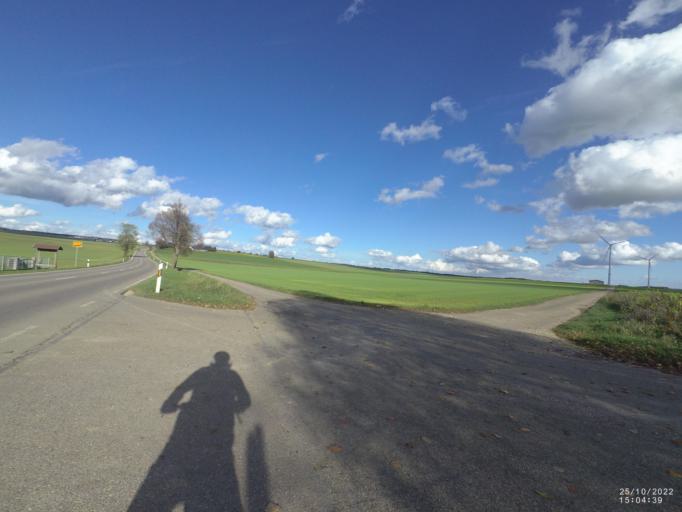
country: DE
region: Baden-Wuerttemberg
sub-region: Regierungsbezirk Stuttgart
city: Bohmenkirch
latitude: 48.6660
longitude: 9.9139
